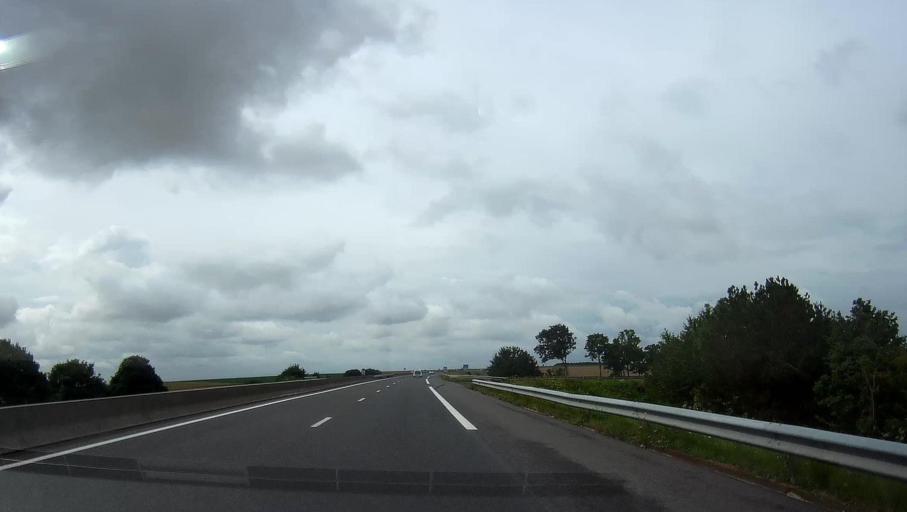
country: FR
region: Champagne-Ardenne
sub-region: Departement de la Marne
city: Compertrix
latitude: 48.8144
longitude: 4.2889
